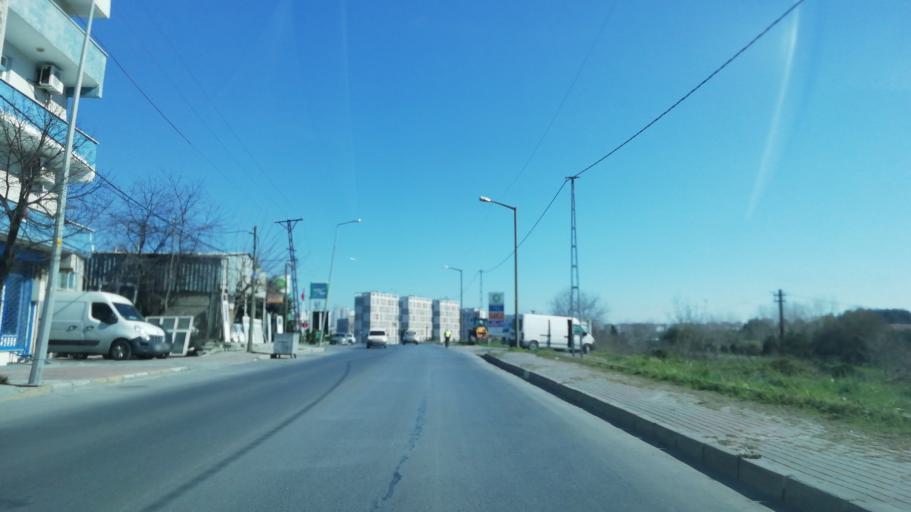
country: TR
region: Istanbul
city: Basaksehir
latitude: 41.0428
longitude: 28.7553
